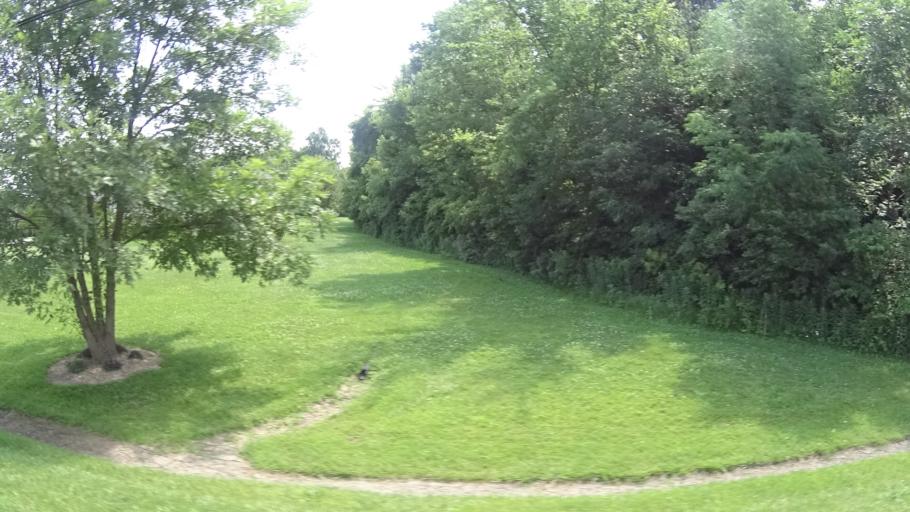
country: US
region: Ohio
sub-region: Lorain County
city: Vermilion
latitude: 41.4025
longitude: -82.4065
